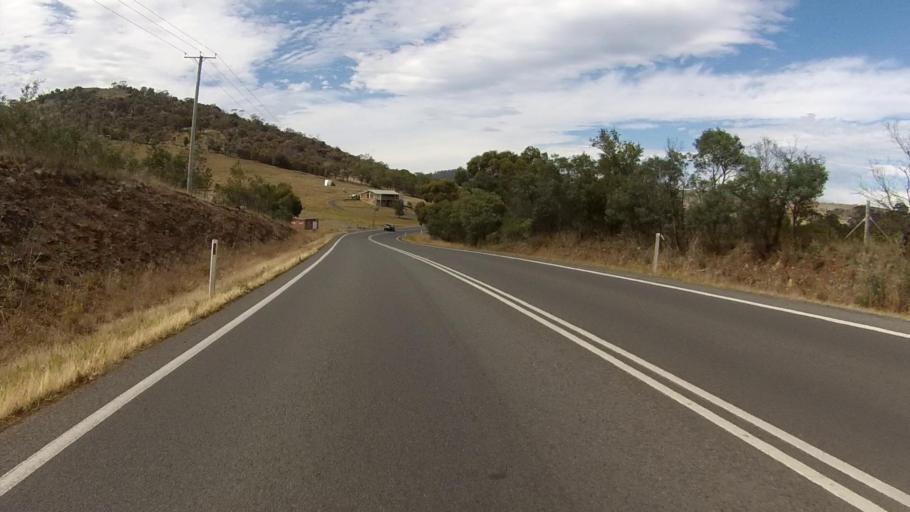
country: AU
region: Tasmania
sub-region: Brighton
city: Old Beach
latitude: -42.6817
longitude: 147.3536
